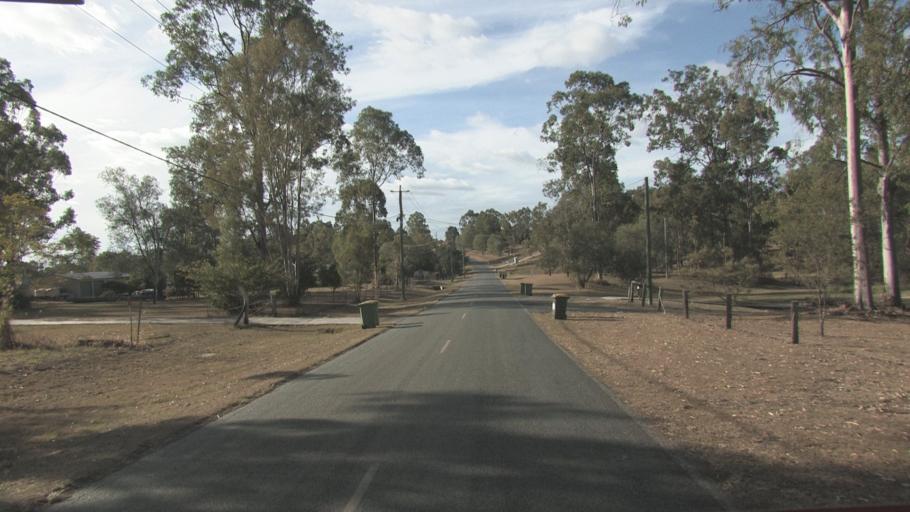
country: AU
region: Queensland
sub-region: Logan
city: Cedar Vale
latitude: -27.8785
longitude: 153.0011
